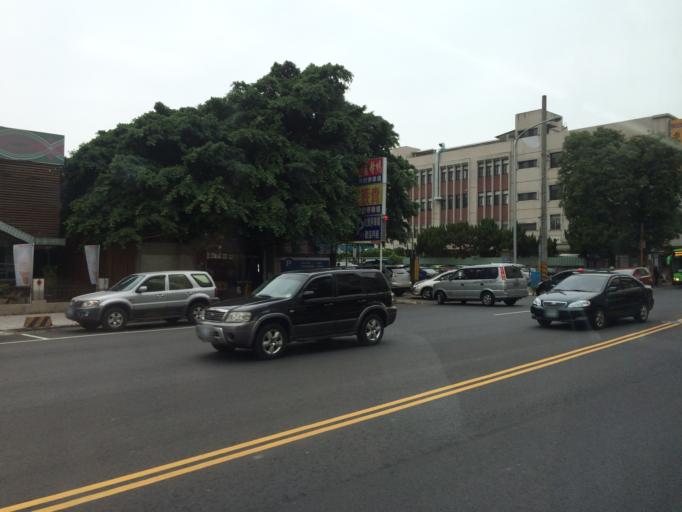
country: TW
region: Taiwan
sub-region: Taichung City
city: Taichung
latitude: 24.1325
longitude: 120.6840
